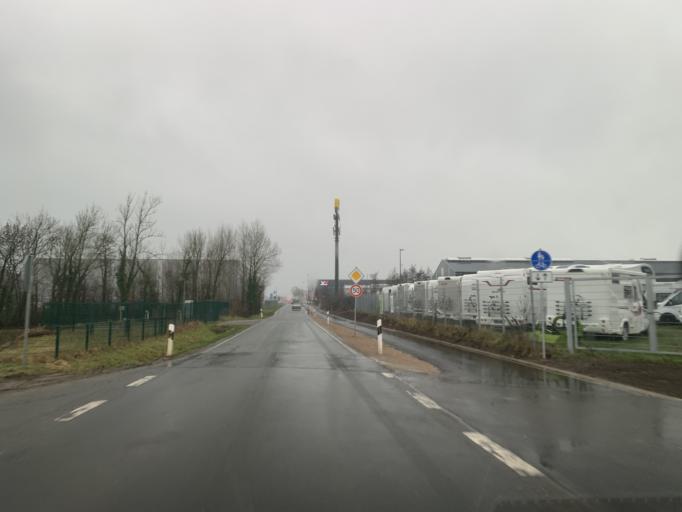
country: DE
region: North Rhine-Westphalia
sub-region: Regierungsbezirk Munster
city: Nottuln
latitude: 51.9131
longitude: 7.4015
